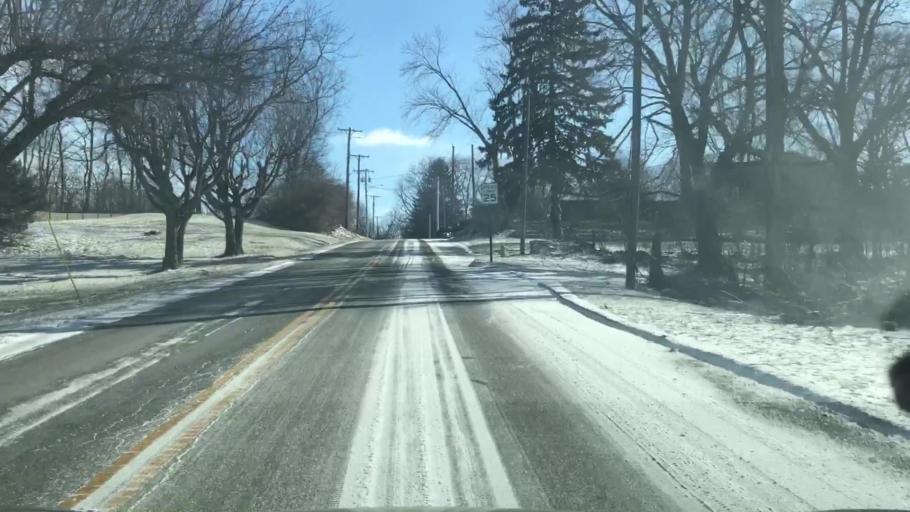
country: US
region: Ohio
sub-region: Greene County
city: Fairborn
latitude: 39.8408
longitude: -84.0148
